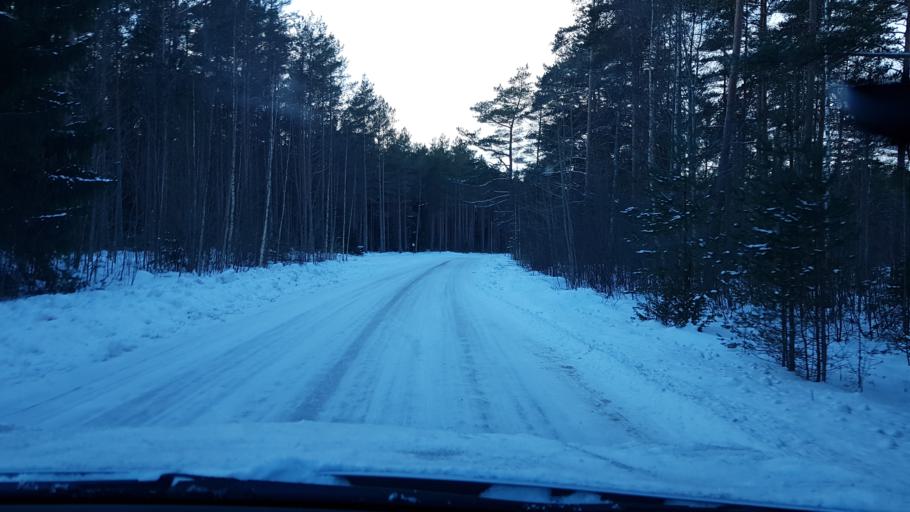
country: EE
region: Harju
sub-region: Nissi vald
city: Turba
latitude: 59.2239
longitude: 24.1580
